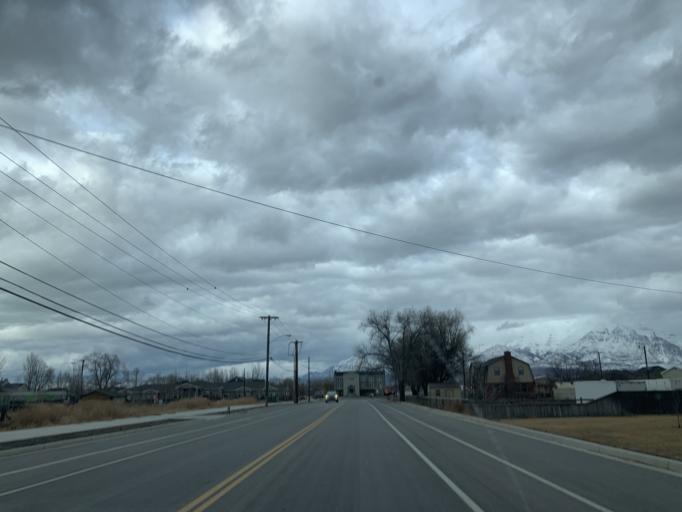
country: US
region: Utah
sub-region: Utah County
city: Provo
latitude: 40.2325
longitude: -111.7130
